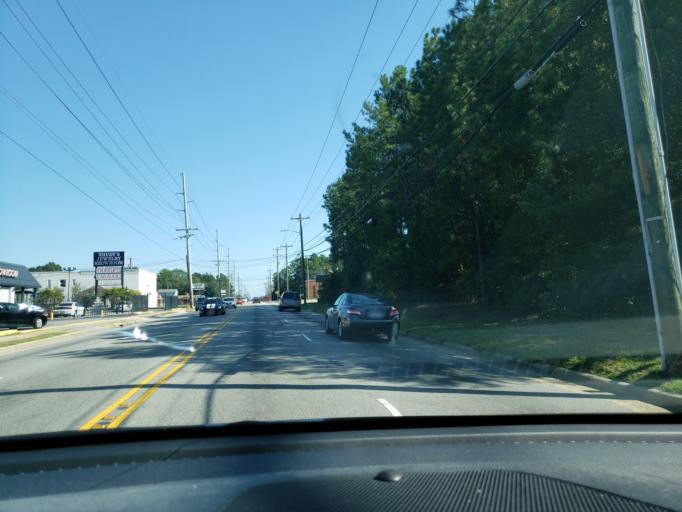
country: US
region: North Carolina
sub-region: Cumberland County
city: Fayetteville
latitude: 35.0883
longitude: -78.9081
